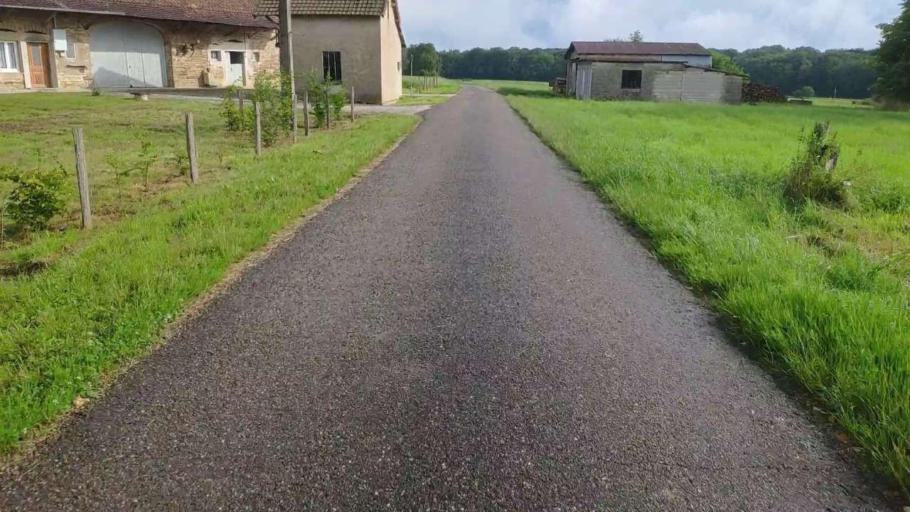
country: FR
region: Franche-Comte
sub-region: Departement du Jura
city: Mont-sous-Vaudrey
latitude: 46.8754
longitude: 5.5221
